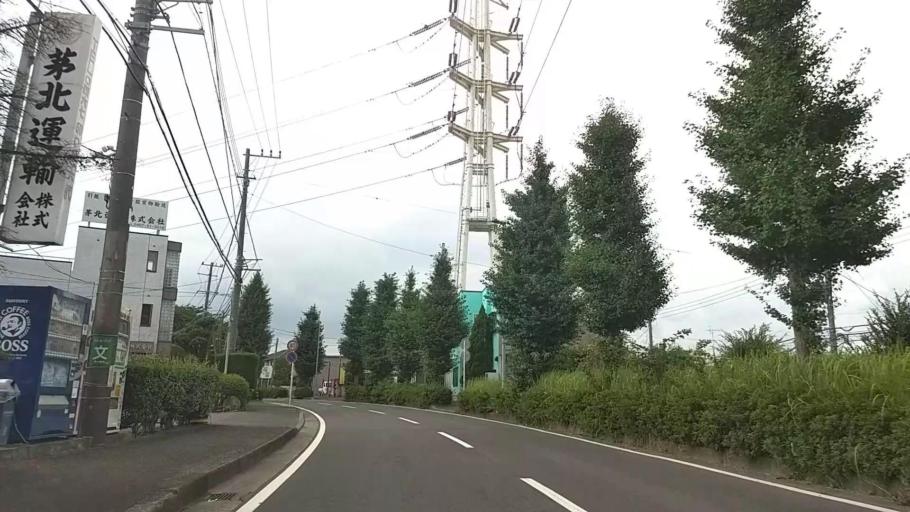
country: JP
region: Kanagawa
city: Fujisawa
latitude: 35.3691
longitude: 139.4315
